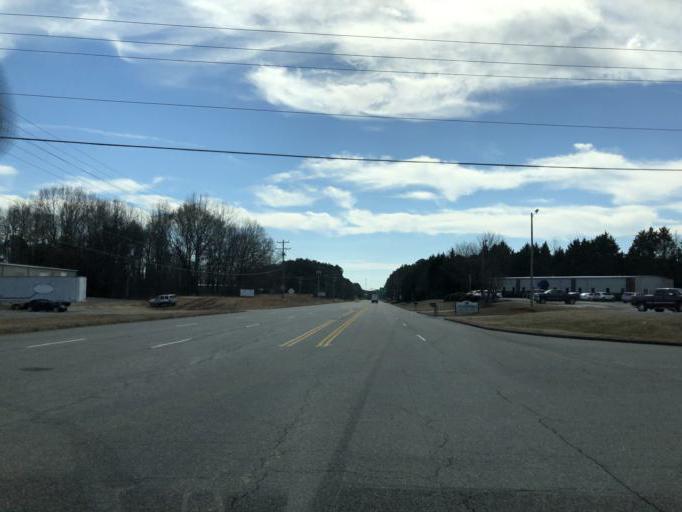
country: US
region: South Carolina
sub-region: Spartanburg County
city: Mayo
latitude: 35.0344
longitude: -81.8791
